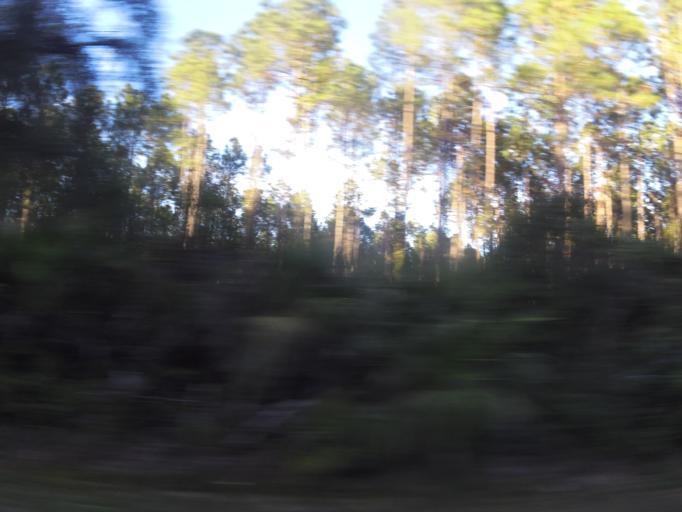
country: US
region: Florida
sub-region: Putnam County
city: East Palatka
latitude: 29.7961
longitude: -81.5217
